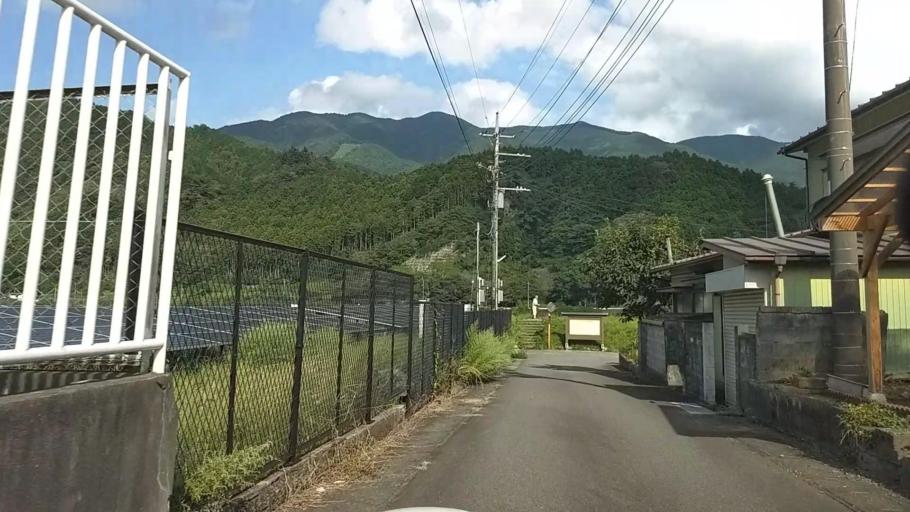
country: JP
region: Shizuoka
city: Fujinomiya
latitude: 35.2896
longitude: 138.4567
